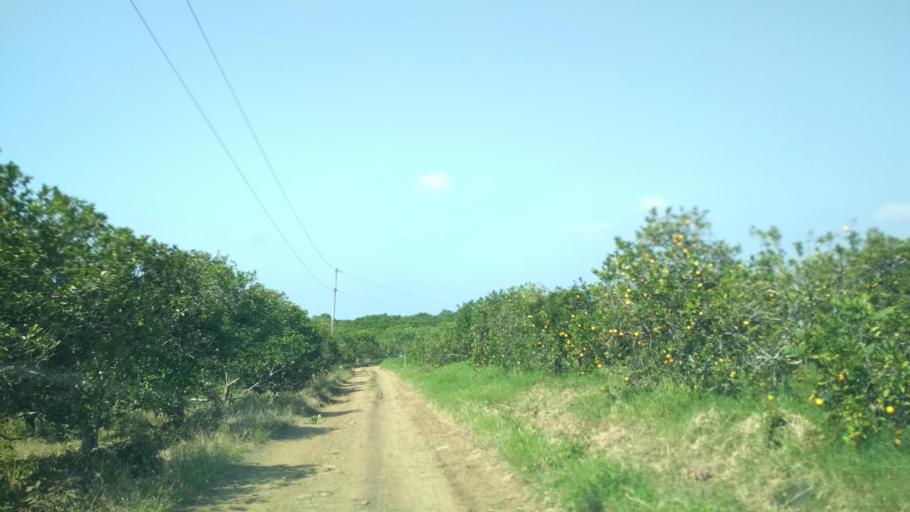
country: MX
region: Puebla
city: San Jose Acateno
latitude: 20.2039
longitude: -97.1808
